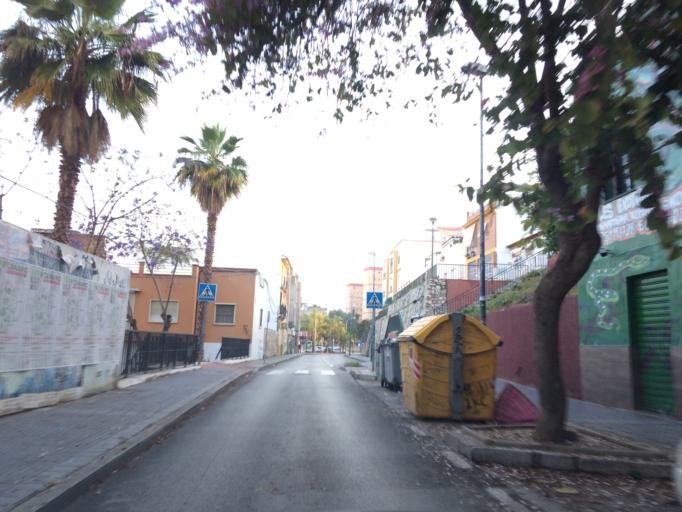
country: ES
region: Andalusia
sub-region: Provincia de Malaga
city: Malaga
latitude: 36.7360
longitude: -4.4228
